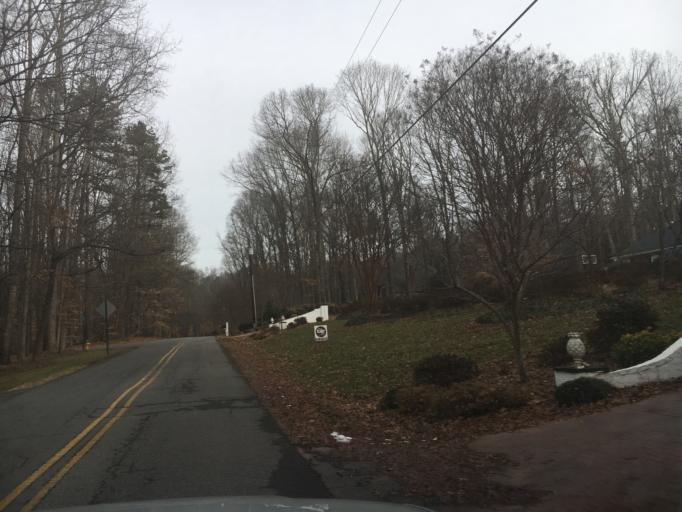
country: US
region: North Carolina
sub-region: Iredell County
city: Statesville
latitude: 35.7894
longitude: -80.8108
